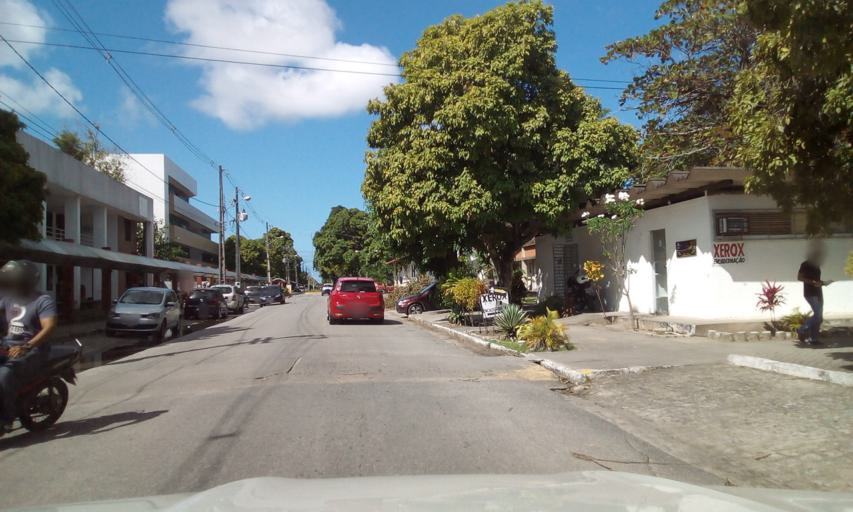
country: BR
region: Paraiba
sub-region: Joao Pessoa
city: Joao Pessoa
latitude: -7.1419
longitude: -34.8502
